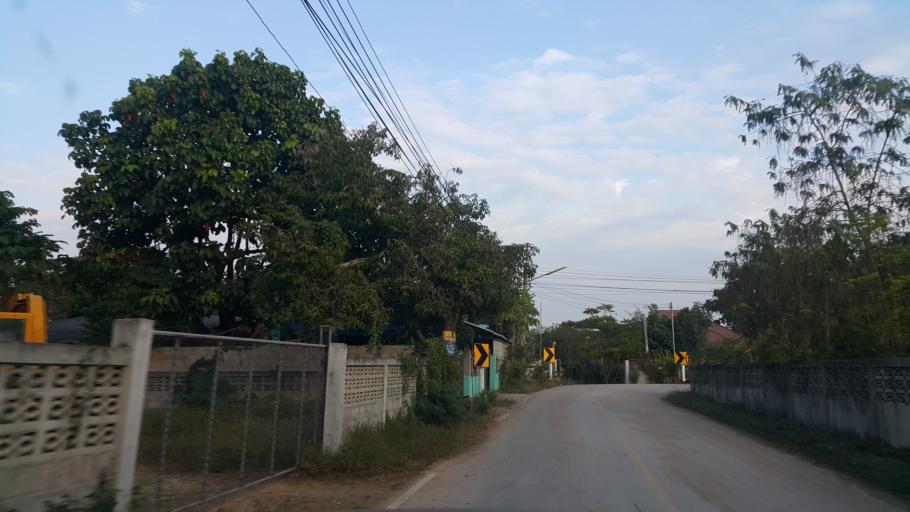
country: TH
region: Lampang
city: Sop Prap
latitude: 17.9011
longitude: 99.3304
